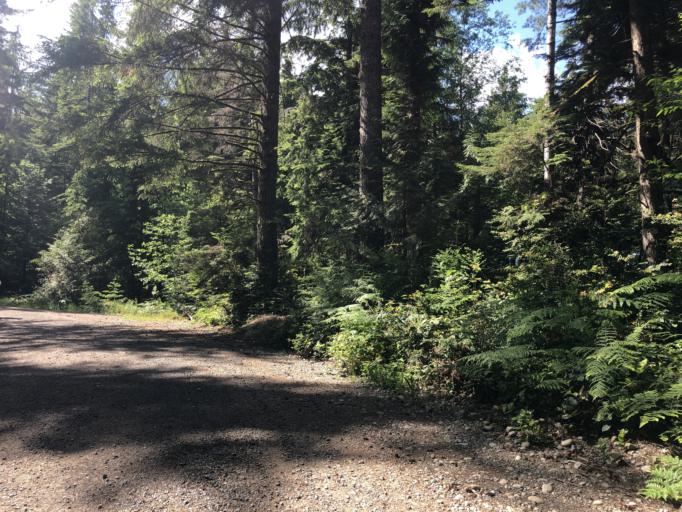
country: US
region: Washington
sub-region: Kitsap County
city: Erlands Point-Kitsap Lake
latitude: 47.5800
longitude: -122.7211
